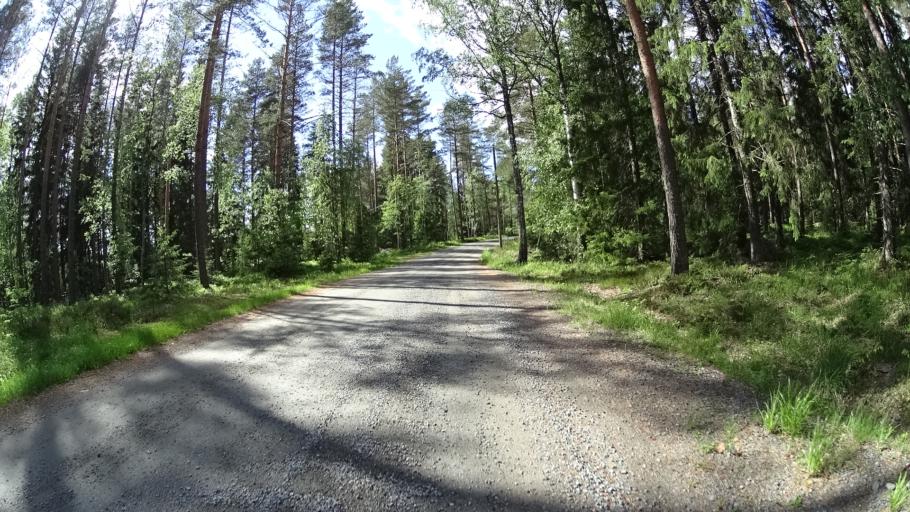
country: FI
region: Uusimaa
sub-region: Raaseporin
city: Pohja
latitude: 60.1855
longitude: 23.5787
